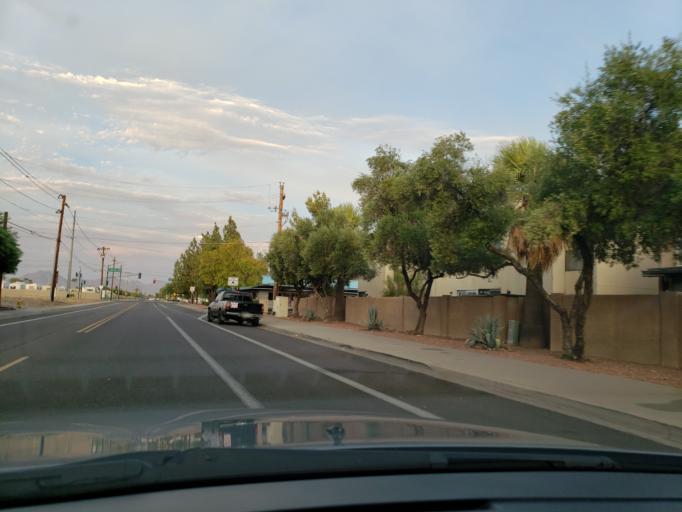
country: US
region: Arizona
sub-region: Maricopa County
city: Paradise Valley
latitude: 33.6336
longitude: -112.0150
